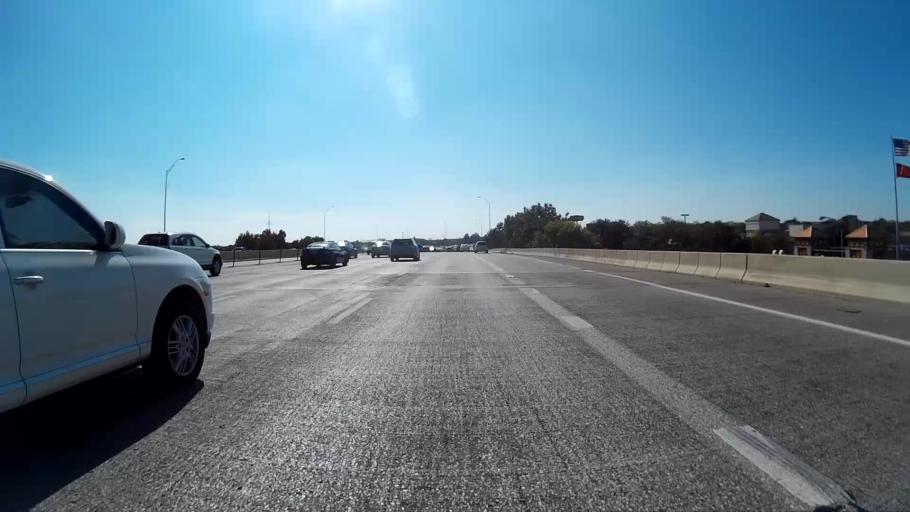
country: US
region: Texas
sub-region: Dallas County
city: Richardson
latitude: 32.9504
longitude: -96.7351
